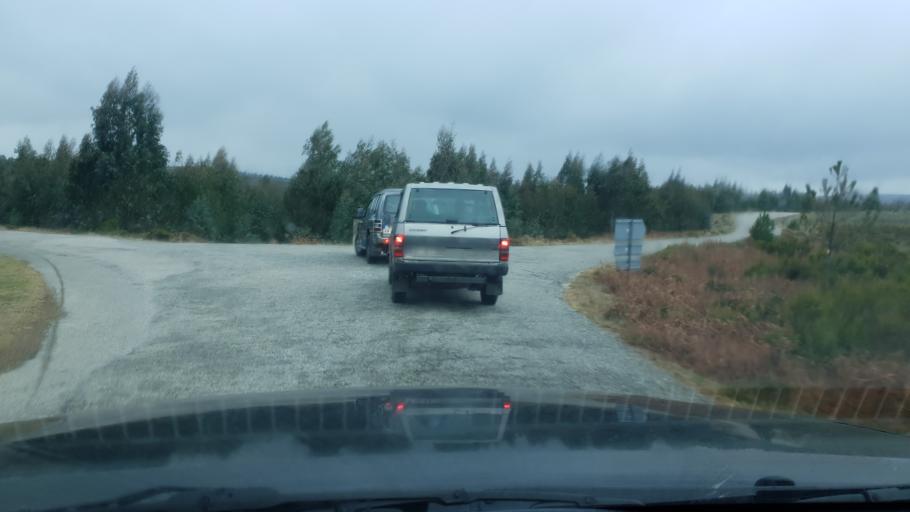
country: PT
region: Viseu
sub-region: Sao Pedro do Sul
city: Sao Pedro do Sul
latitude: 40.8685
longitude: -8.0838
